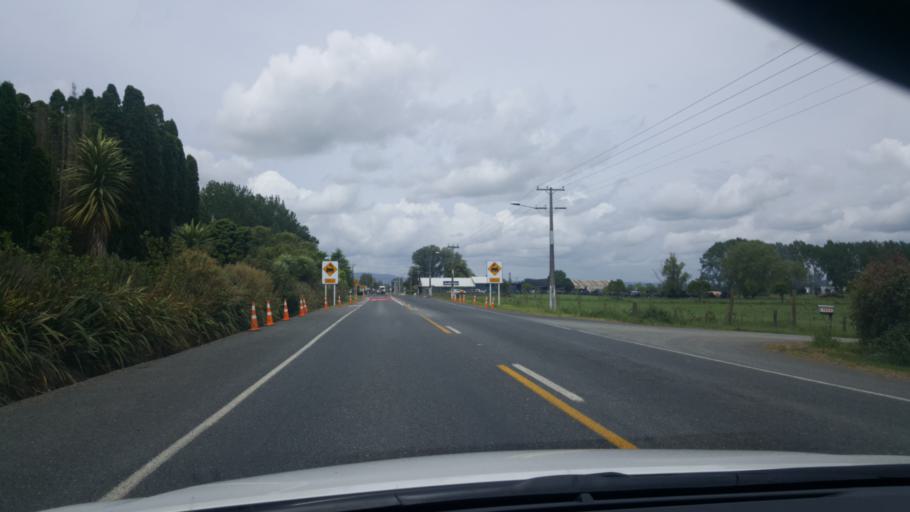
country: NZ
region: Waikato
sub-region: Matamata-Piako District
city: Matamata
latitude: -37.8807
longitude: 175.7573
